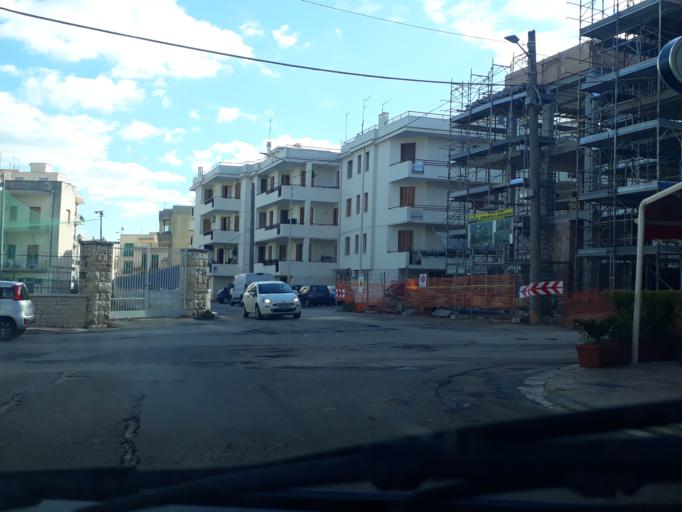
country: IT
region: Apulia
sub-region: Provincia di Brindisi
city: Fasano
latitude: 40.8342
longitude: 17.3544
